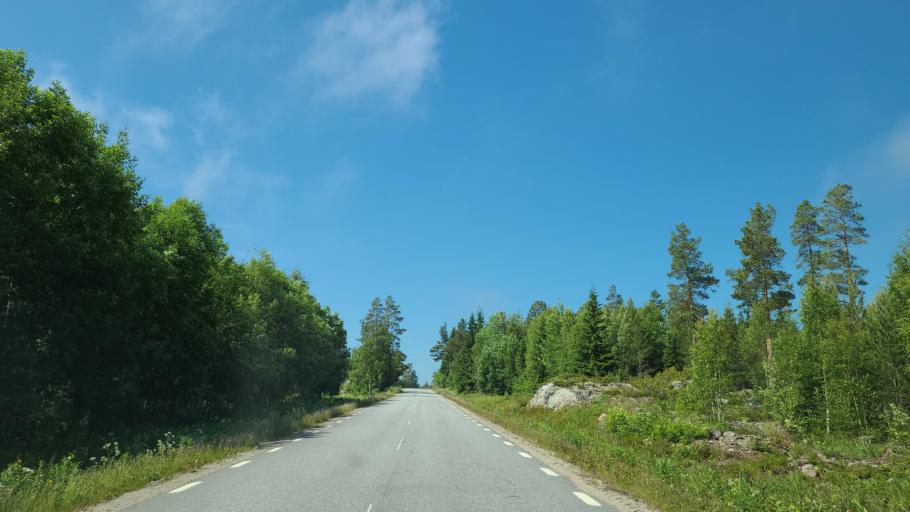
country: SE
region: Vaesternorrland
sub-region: OErnskoeldsviks Kommun
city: Husum
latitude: 63.4803
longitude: 19.2162
